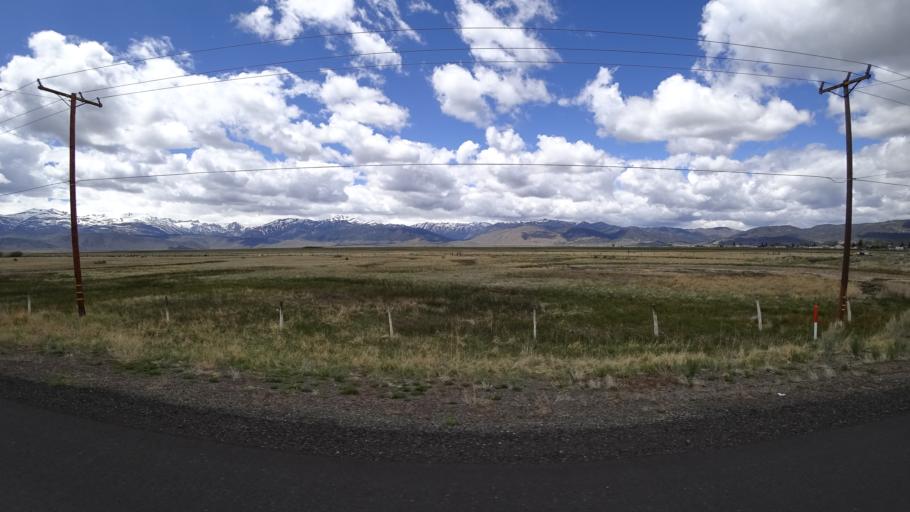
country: US
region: California
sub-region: Mono County
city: Bridgeport
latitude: 38.2480
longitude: -119.2209
